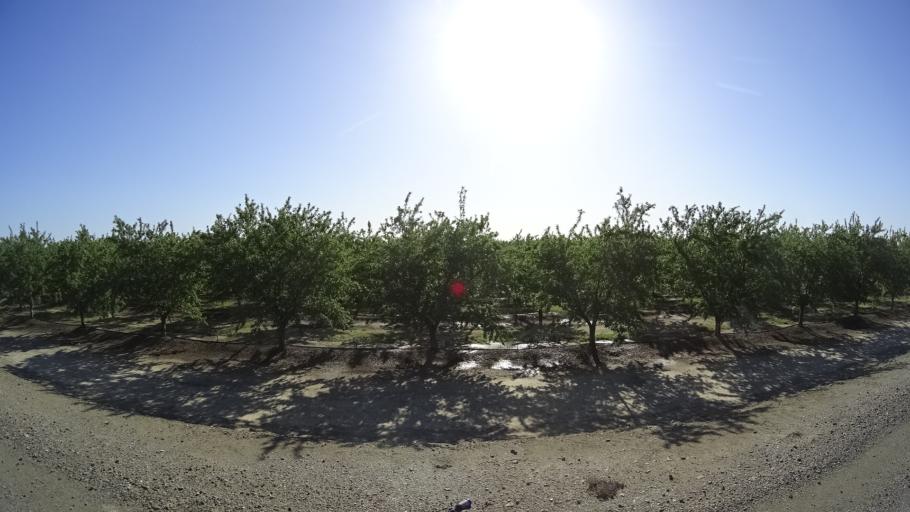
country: US
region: California
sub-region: Glenn County
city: Orland
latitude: 39.6911
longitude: -122.1220
